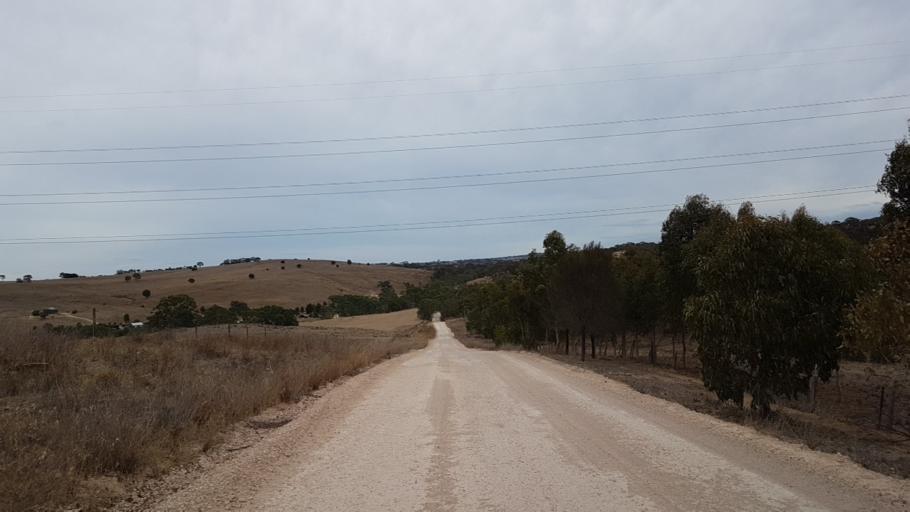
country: AU
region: South Australia
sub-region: Mount Barker
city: Callington
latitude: -35.0086
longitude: 139.0397
